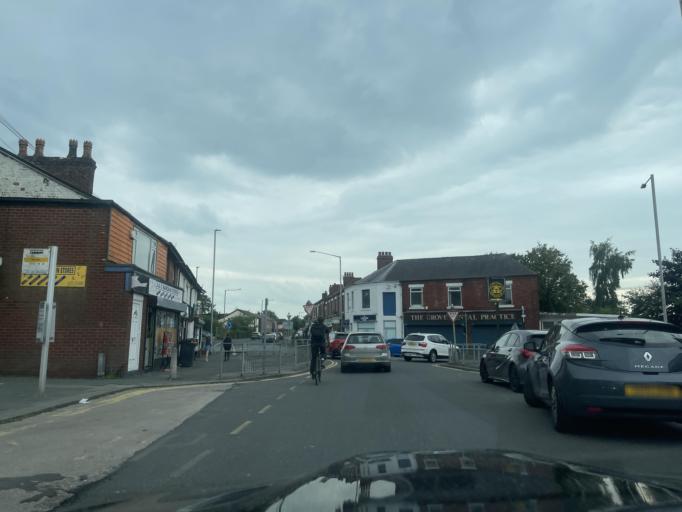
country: GB
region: England
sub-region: Lancashire
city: Leyland
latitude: 53.6894
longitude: -2.7166
